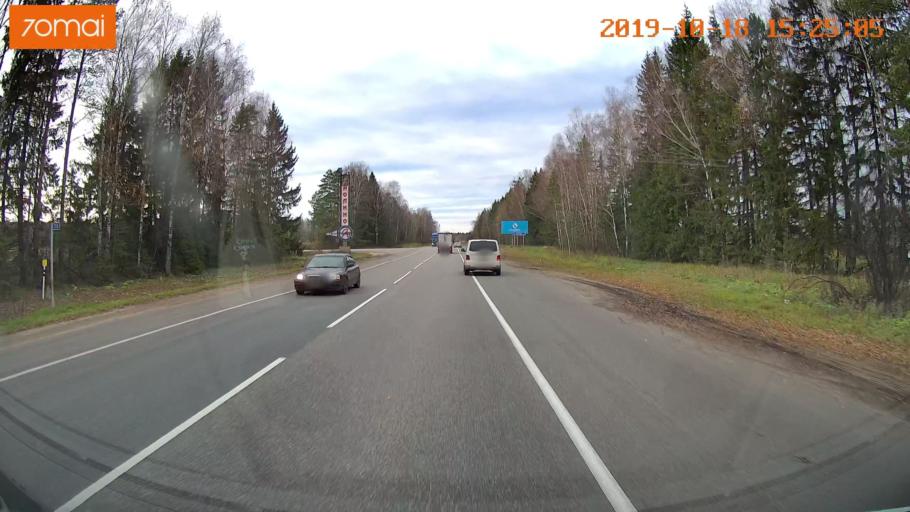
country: RU
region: Vladimir
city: Anopino
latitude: 55.7388
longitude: 40.7123
